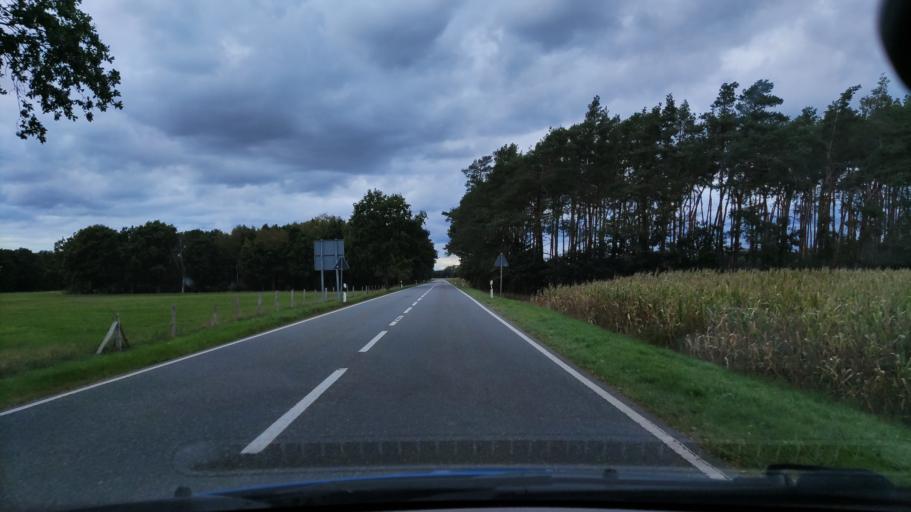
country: DE
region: Lower Saxony
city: Neu Darchau
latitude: 53.3033
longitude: 10.9688
